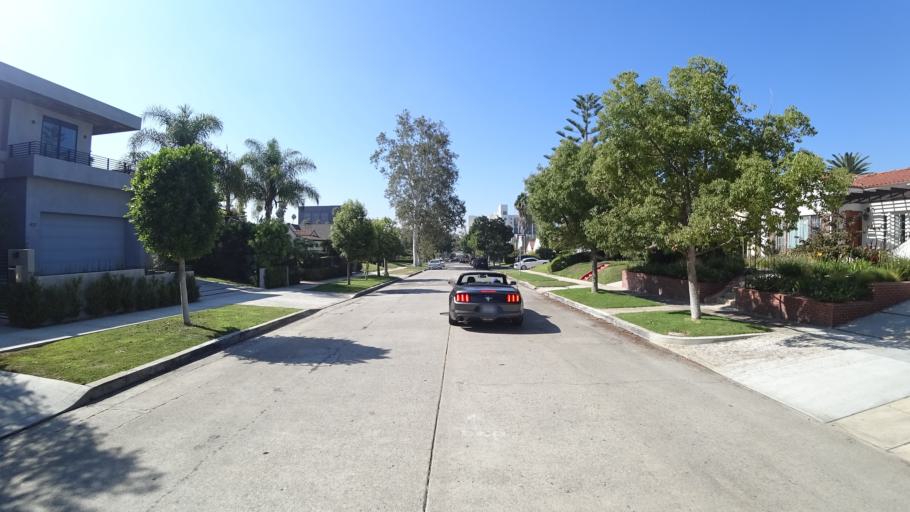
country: US
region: California
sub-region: Los Angeles County
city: West Hollywood
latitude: 34.0661
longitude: -118.3397
